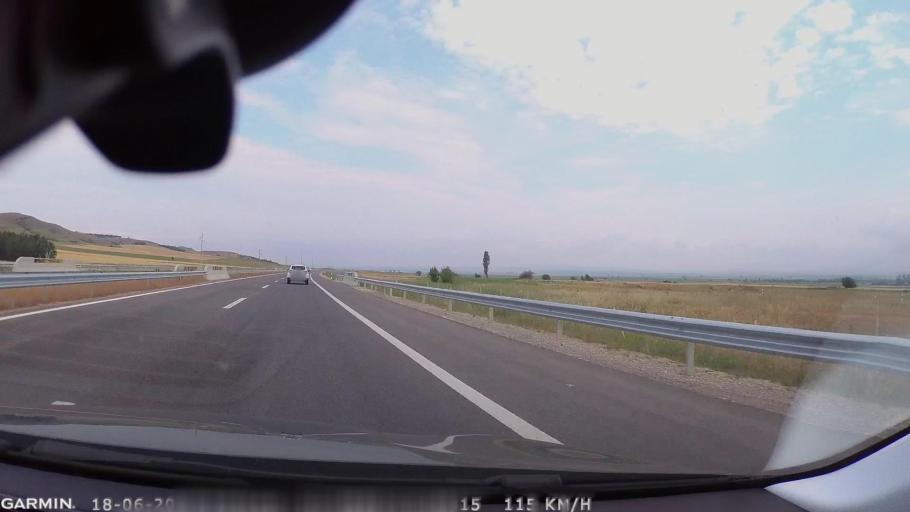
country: MK
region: Stip
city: Shtip
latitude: 41.7984
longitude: 22.0826
